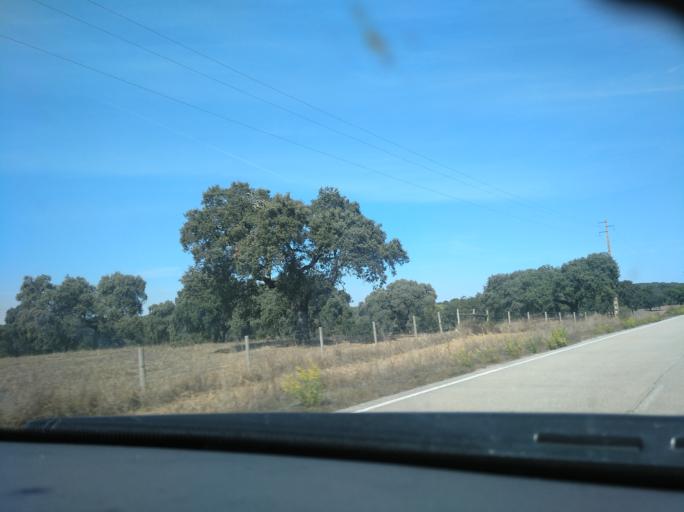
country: PT
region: Evora
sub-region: Arraiolos
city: Arraiolos
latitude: 38.6826
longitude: -8.0917
